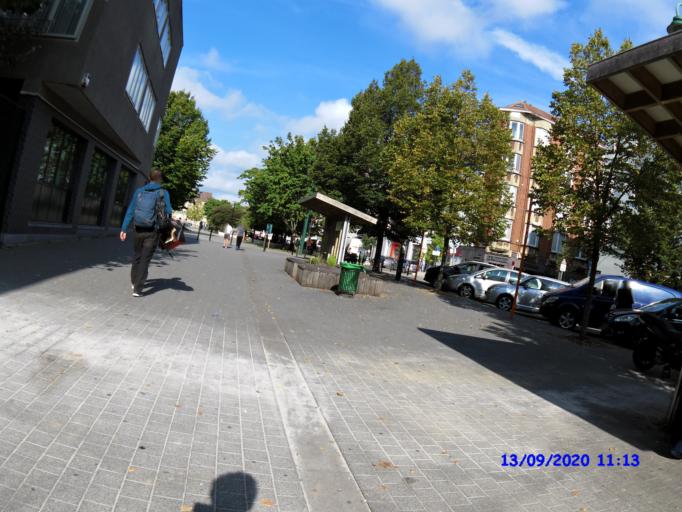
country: BE
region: Brussels Capital
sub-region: Bruxelles-Capitale
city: Brussels
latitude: 50.8558
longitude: 4.3383
